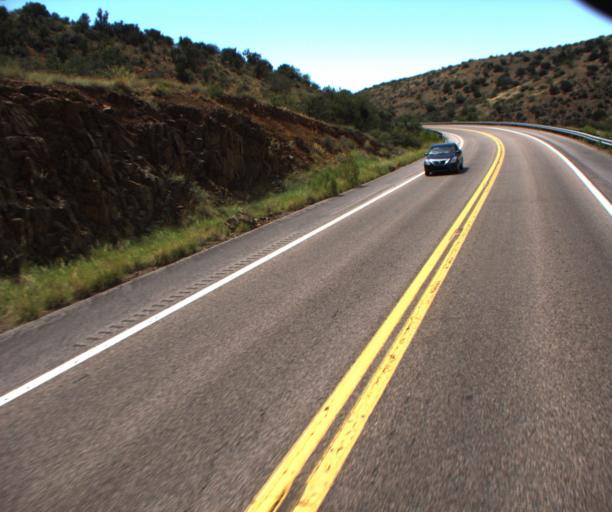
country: US
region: Arizona
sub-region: Gila County
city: Globe
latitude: 33.4769
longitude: -110.7230
